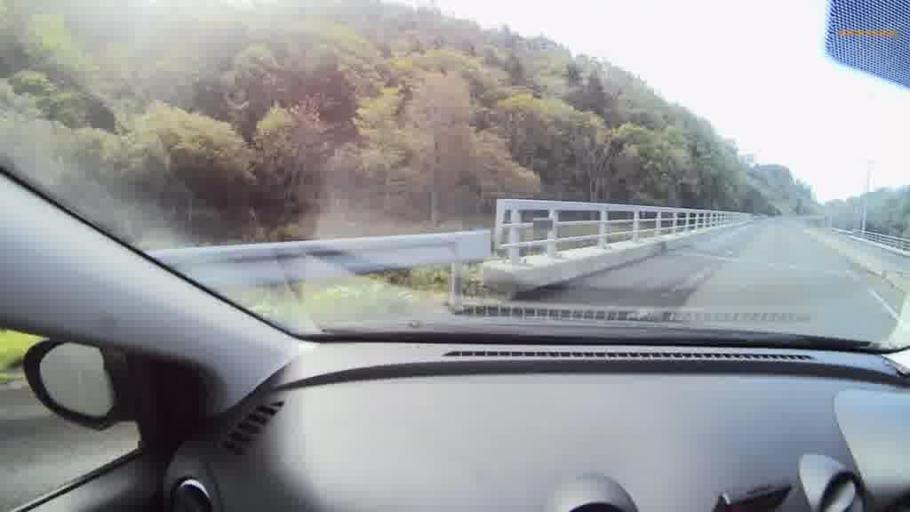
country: JP
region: Hokkaido
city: Kushiro
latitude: 43.0083
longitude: 144.5104
